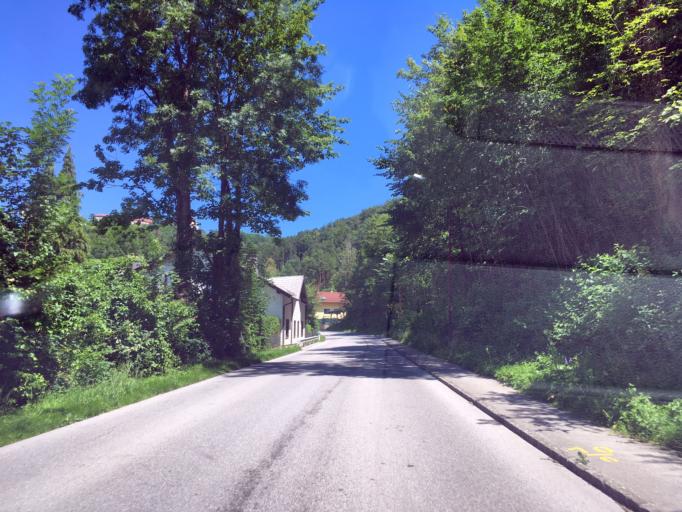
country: AT
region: Lower Austria
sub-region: Politischer Bezirk Neunkirchen
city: Pitten
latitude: 47.7117
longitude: 16.1853
